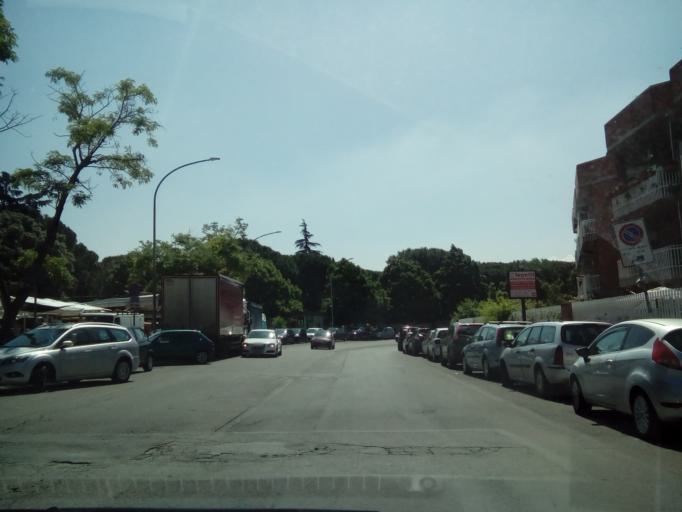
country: IT
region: Latium
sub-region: Citta metropolitana di Roma Capitale
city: Rome
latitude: 41.8858
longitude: 12.5882
